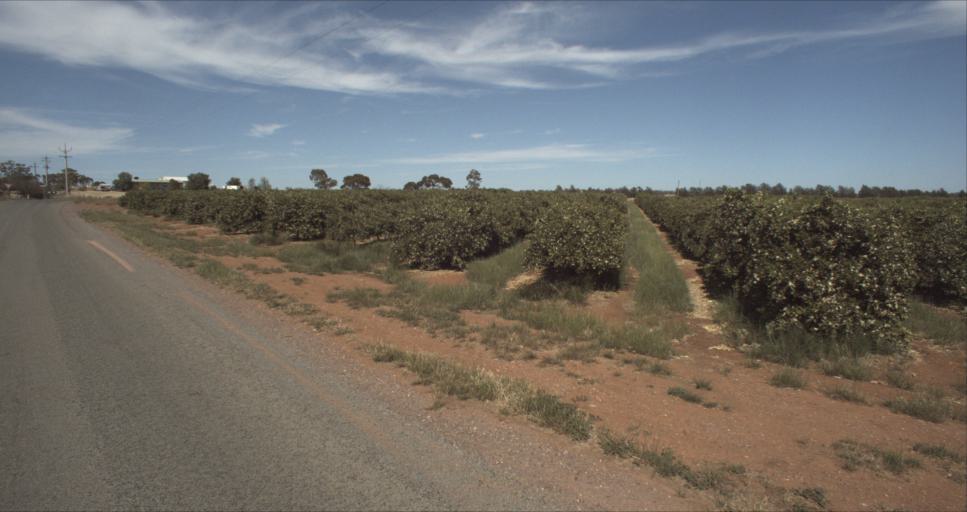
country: AU
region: New South Wales
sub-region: Leeton
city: Leeton
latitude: -34.5919
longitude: 146.4724
